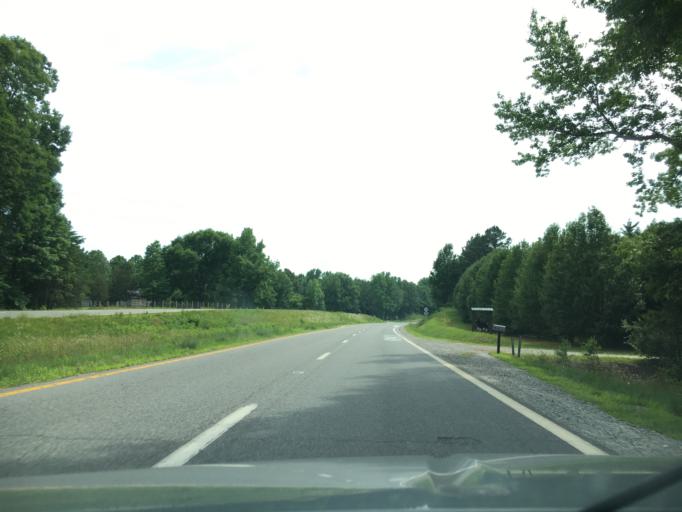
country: US
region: Virginia
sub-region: Prince Edward County
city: Hampden Sydney
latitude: 37.0931
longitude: -78.3802
